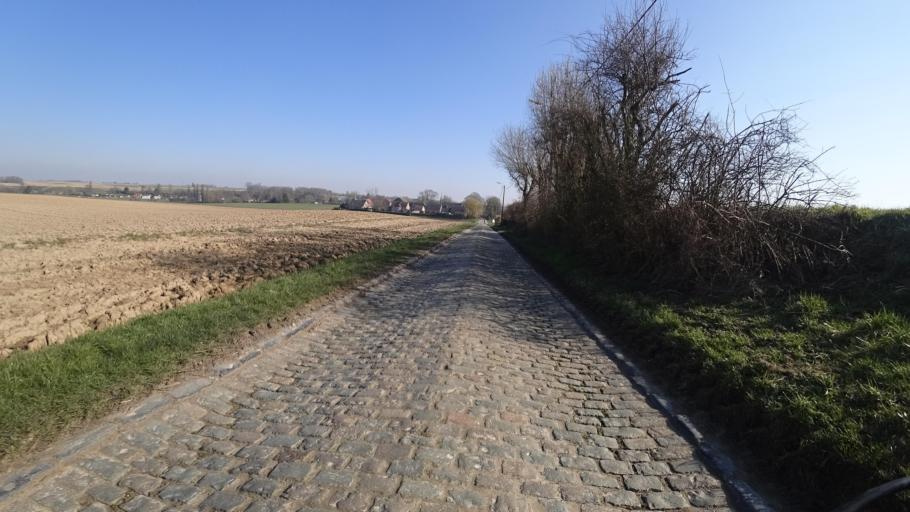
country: BE
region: Wallonia
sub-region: Province du Brabant Wallon
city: Mont-Saint-Guibert
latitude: 50.6043
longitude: 4.6005
